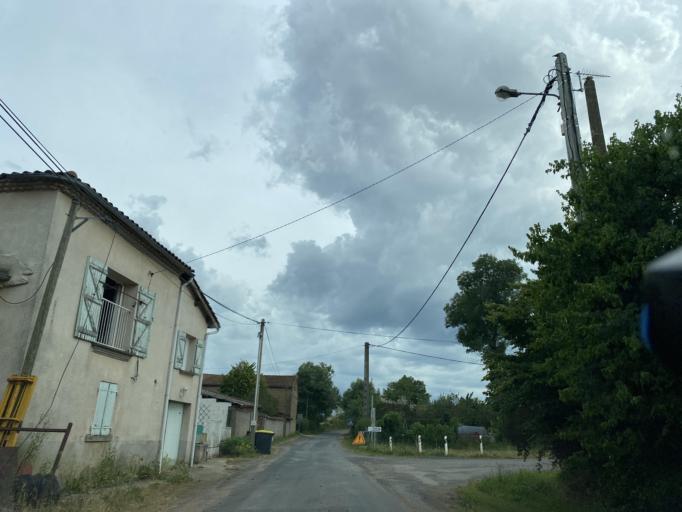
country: FR
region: Auvergne
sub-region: Departement du Puy-de-Dome
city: Courpiere
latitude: 45.7416
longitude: 3.4540
